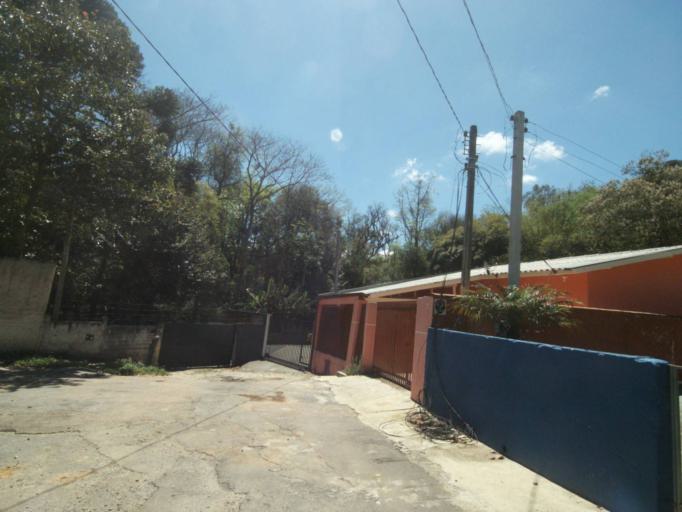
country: BR
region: Parana
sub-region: Curitiba
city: Curitiba
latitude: -25.3929
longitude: -49.2659
